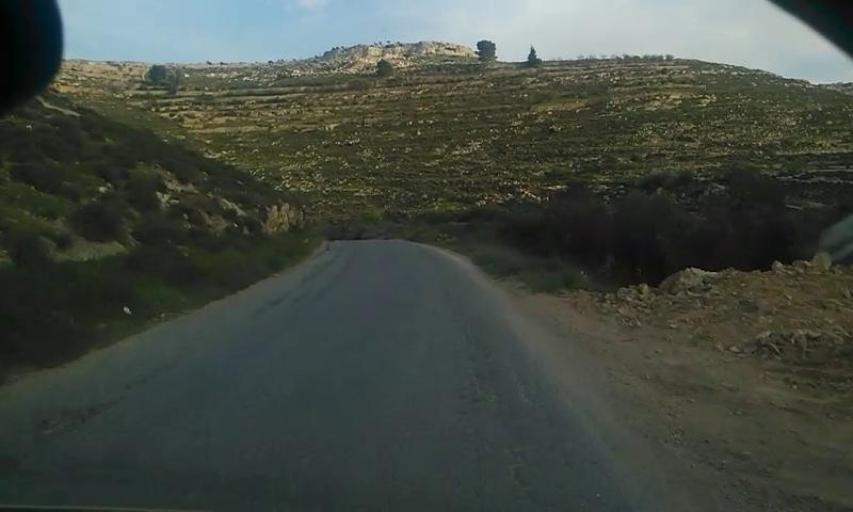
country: PS
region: West Bank
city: Ash Shuyukh
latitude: 31.5964
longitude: 35.1758
